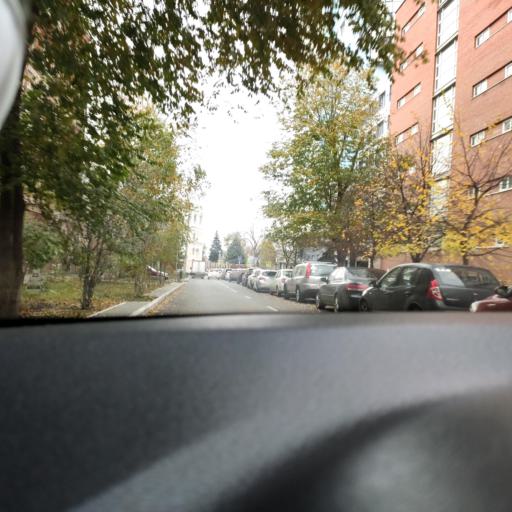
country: RU
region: Samara
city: Samara
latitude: 53.1995
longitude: 50.1024
